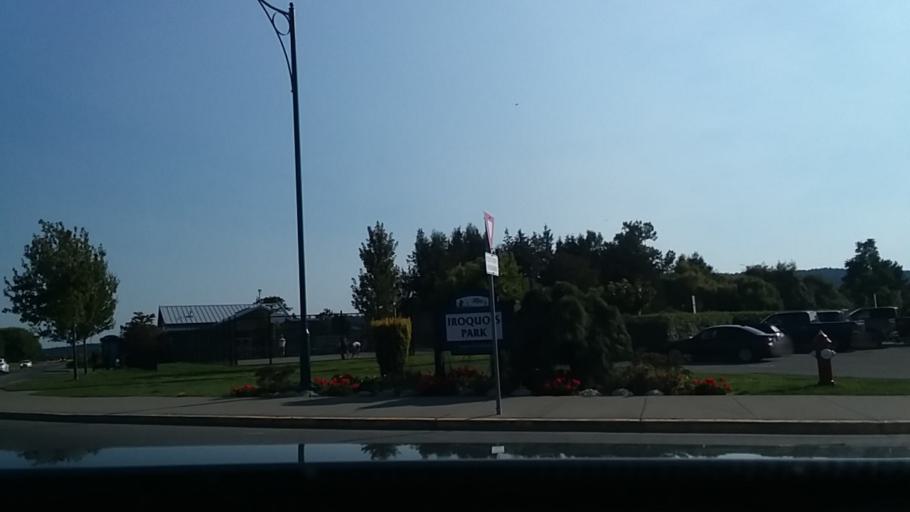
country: CA
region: British Columbia
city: North Saanich
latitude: 48.6444
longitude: -123.4005
